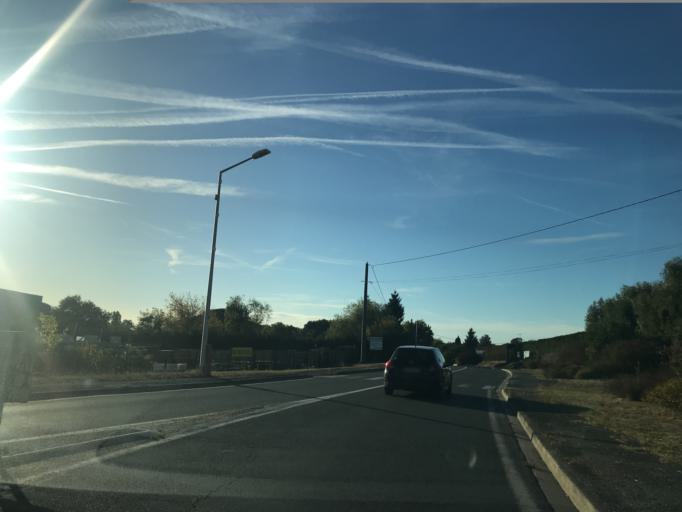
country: FR
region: Poitou-Charentes
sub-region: Departement de la Charente-Maritime
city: Montguyon
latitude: 45.2124
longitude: -0.1765
